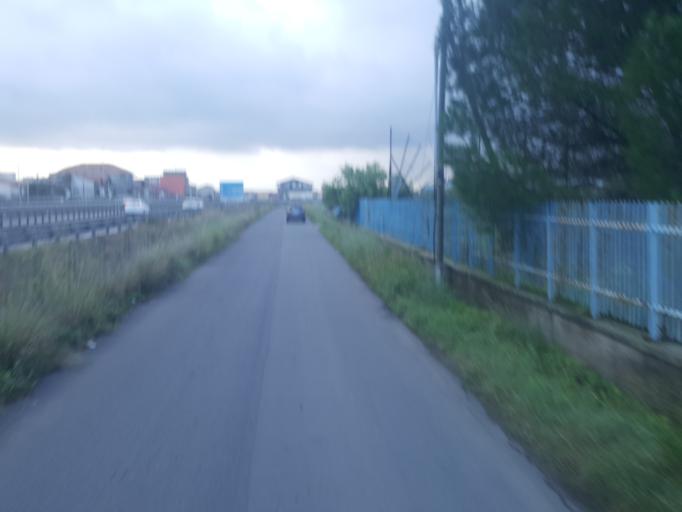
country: IT
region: Sicily
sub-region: Catania
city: Belvedere-Piano Tavola
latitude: 37.5369
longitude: 14.9764
